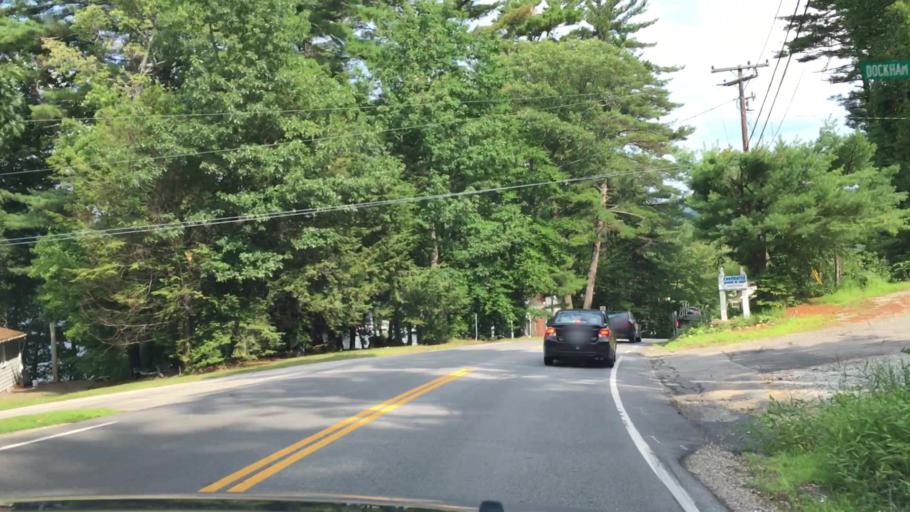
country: US
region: New Hampshire
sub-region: Belknap County
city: Gilford
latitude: 43.5836
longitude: -71.4130
